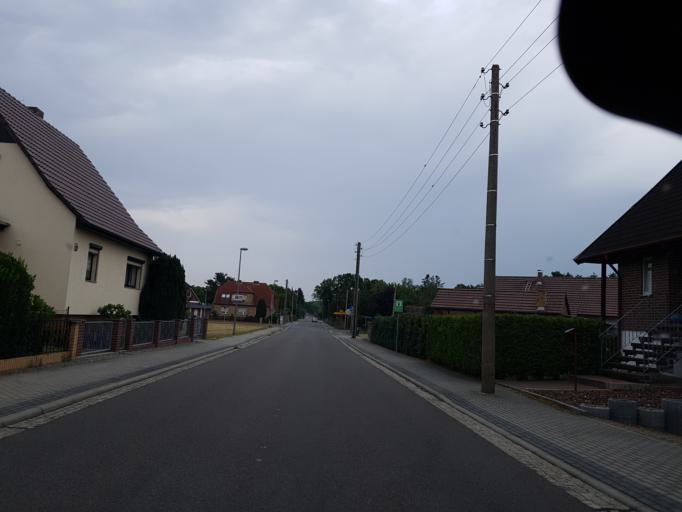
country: DE
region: Brandenburg
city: Schipkau
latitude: 51.5505
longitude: 13.9199
